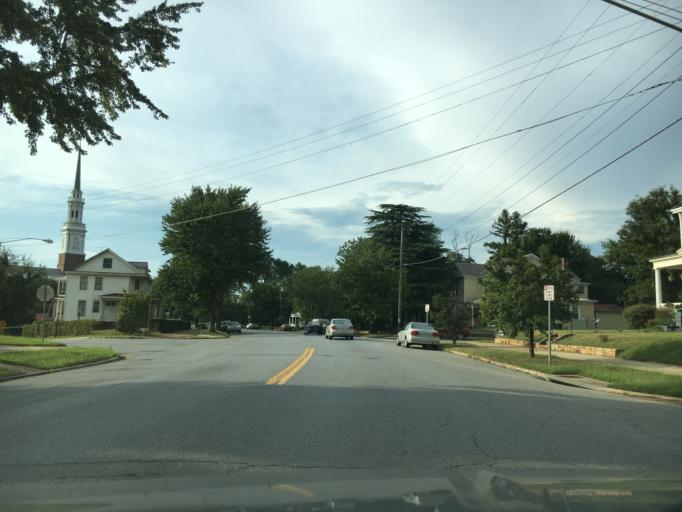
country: US
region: Virginia
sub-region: City of Lynchburg
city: Lynchburg
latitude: 37.4304
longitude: -79.1544
